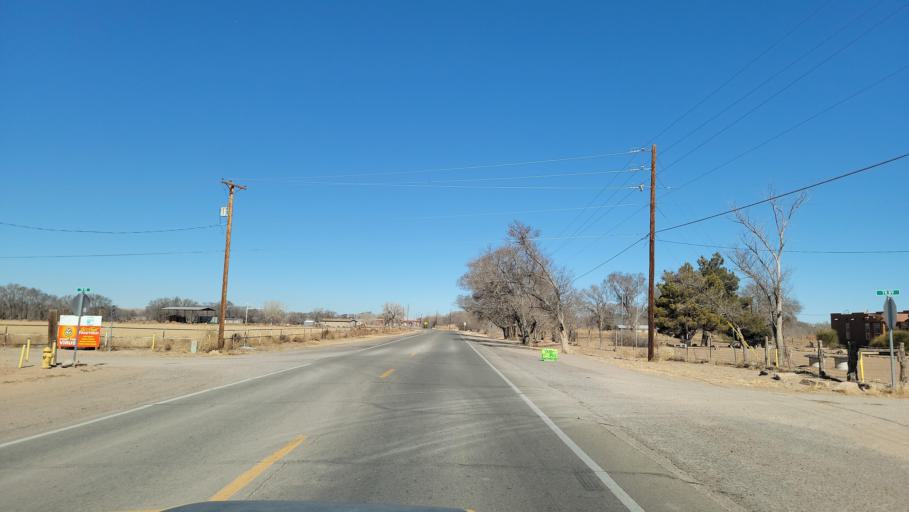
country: US
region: New Mexico
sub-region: Bernalillo County
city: South Valley
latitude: 34.9421
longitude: -106.6922
